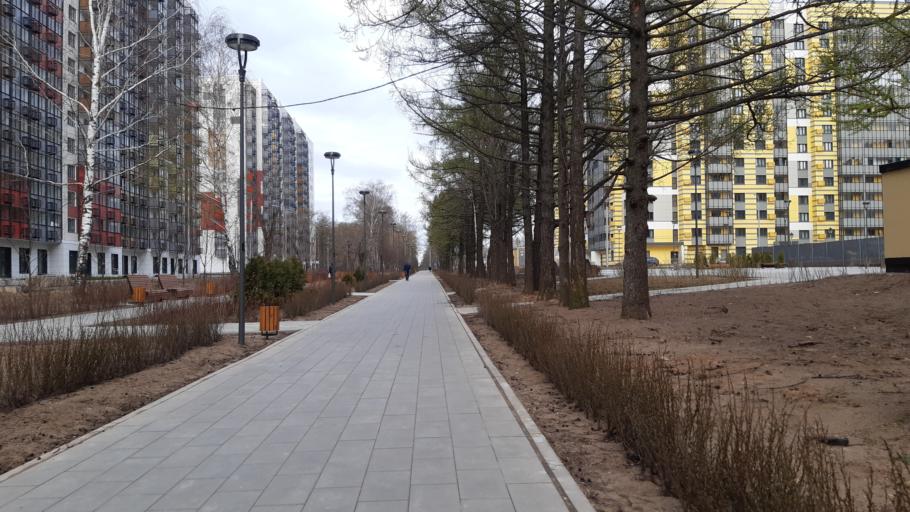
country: RU
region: Moscow
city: Severnyy
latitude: 55.9413
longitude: 37.5264
